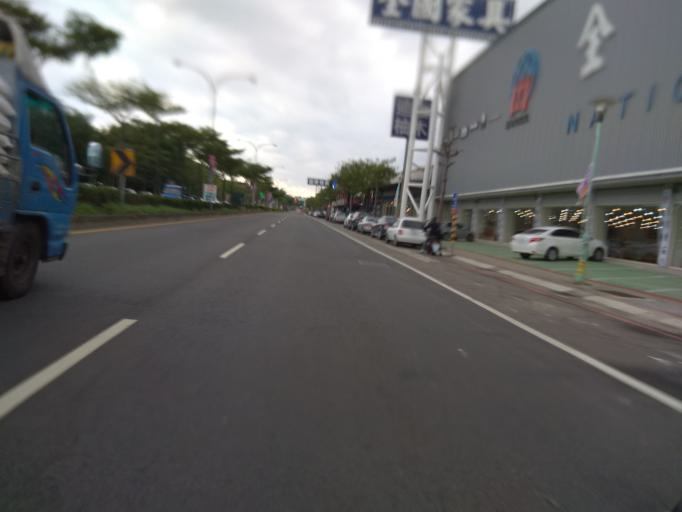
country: TW
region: Taiwan
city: Daxi
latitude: 24.9381
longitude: 121.2161
